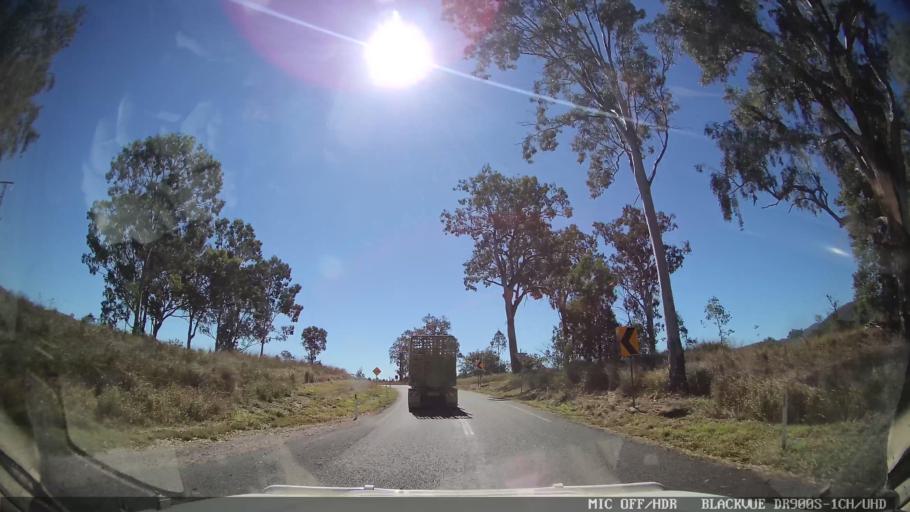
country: AU
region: Queensland
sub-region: Gladstone
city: Toolooa
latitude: -24.2737
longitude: 151.2761
